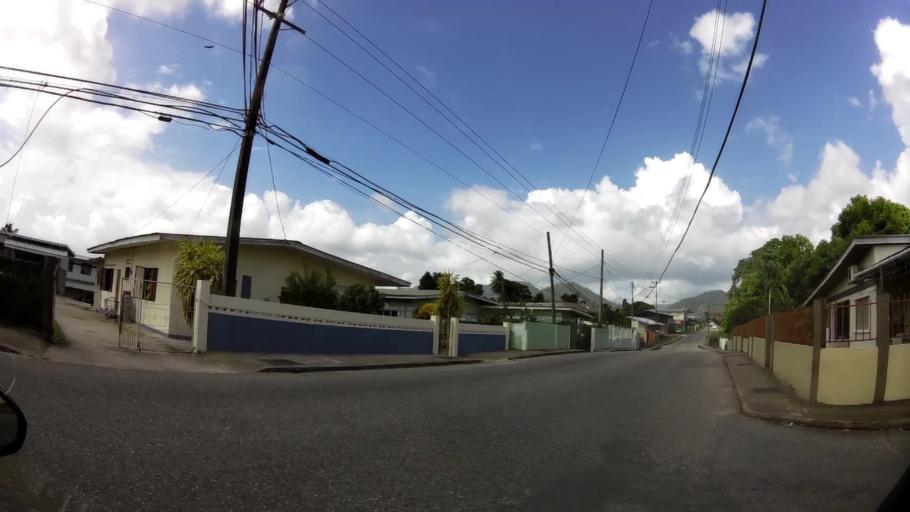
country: TT
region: Borough of Arima
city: Arima
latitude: 10.6310
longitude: -61.2816
